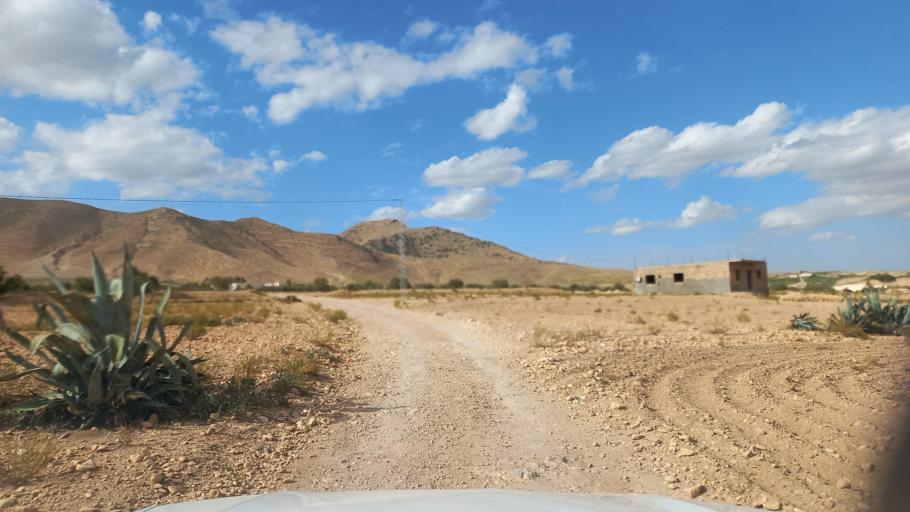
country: TN
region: Al Qasrayn
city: Sbiba
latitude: 35.4494
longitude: 9.0756
